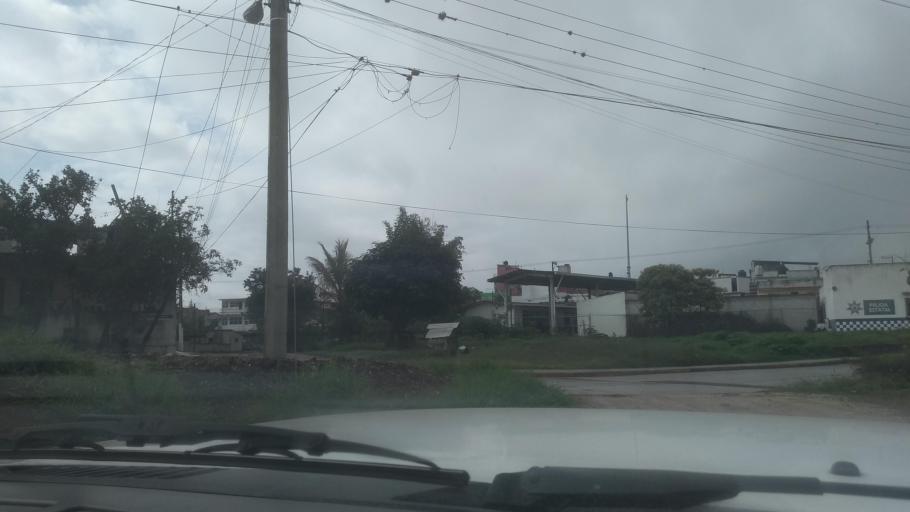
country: MX
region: Veracruz
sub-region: Xalapa
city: Colonia Santa Barbara
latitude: 19.5066
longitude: -96.8742
